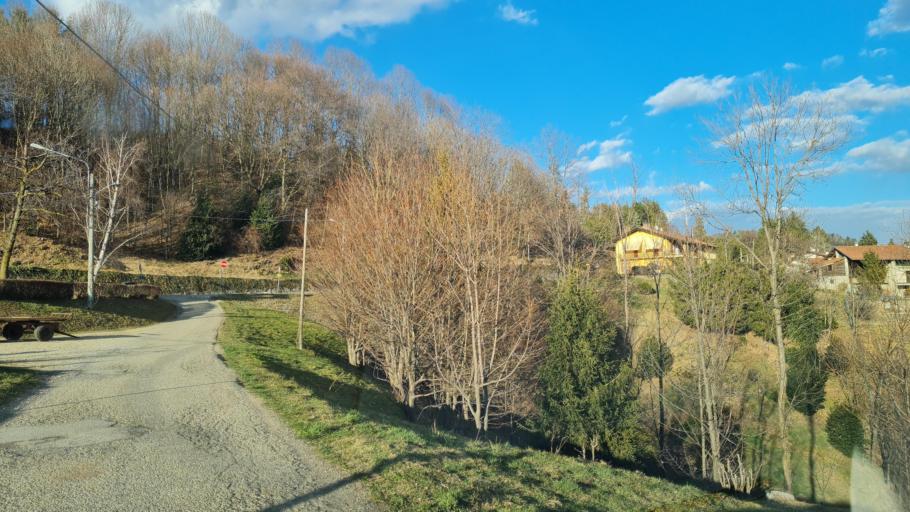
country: IT
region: Piedmont
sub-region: Provincia di Biella
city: Pollone
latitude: 45.5784
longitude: 7.9897
